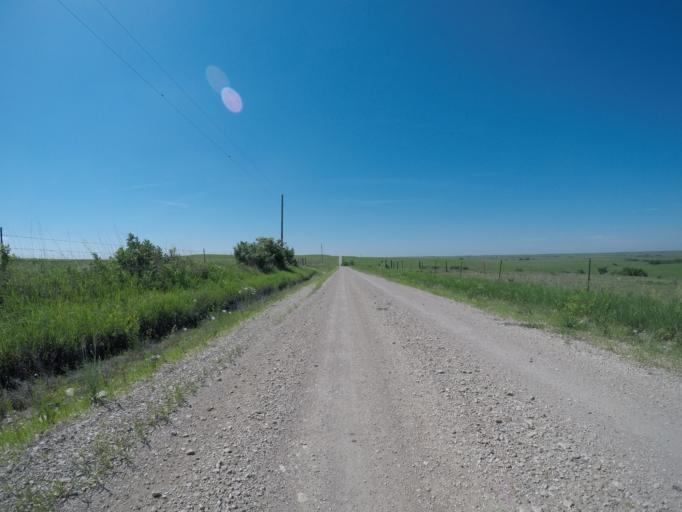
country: US
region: Kansas
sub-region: Wabaunsee County
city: Alma
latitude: 39.0082
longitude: -96.1783
